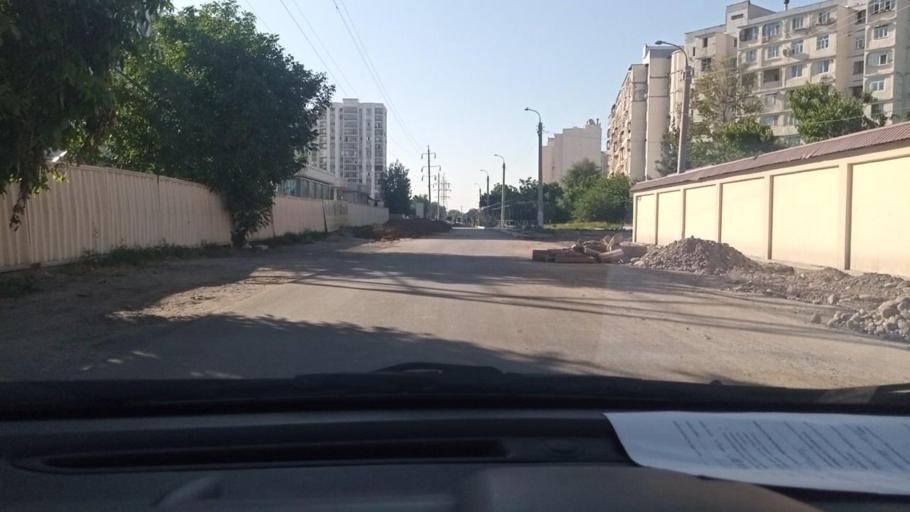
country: UZ
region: Toshkent
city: Salor
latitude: 41.3231
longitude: 69.3581
